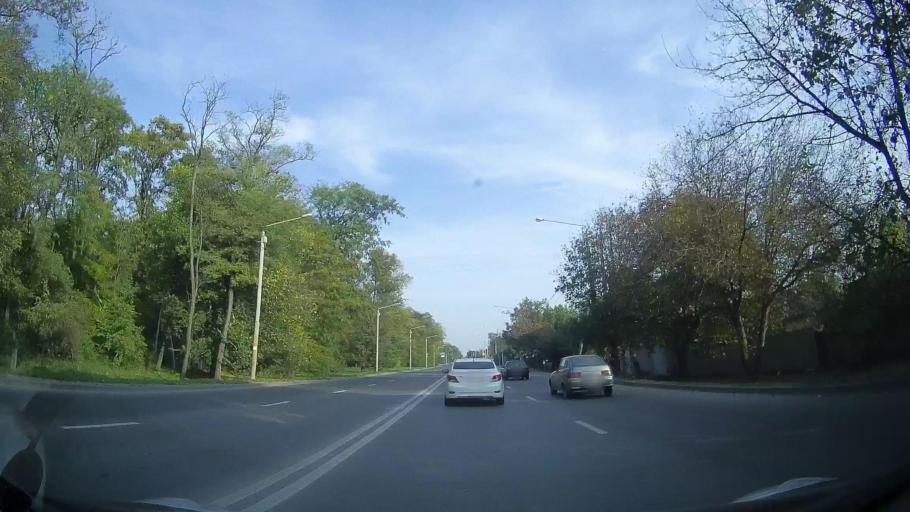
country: RU
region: Rostov
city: Imeni Chkalova
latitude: 47.2757
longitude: 39.7892
